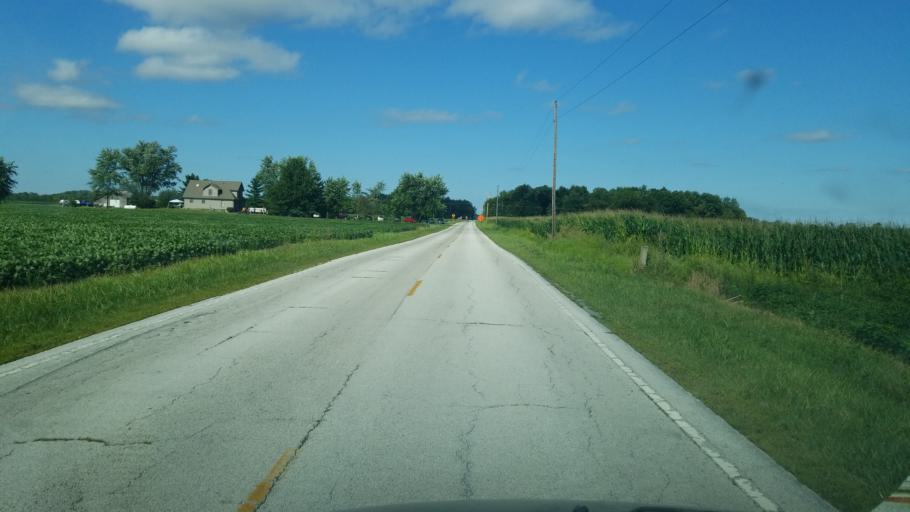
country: US
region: Ohio
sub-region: Seneca County
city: Fostoria
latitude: 41.1081
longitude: -83.4729
